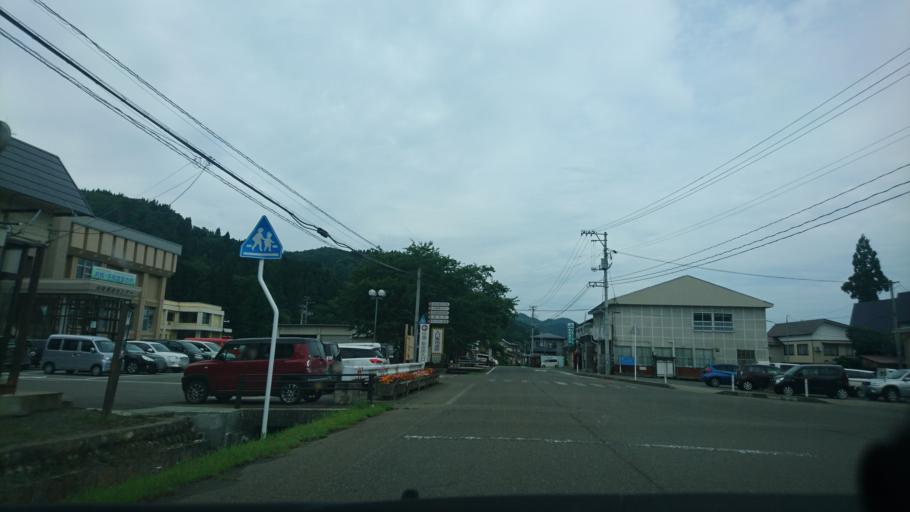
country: JP
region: Akita
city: Yuzawa
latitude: 39.1796
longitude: 140.6493
